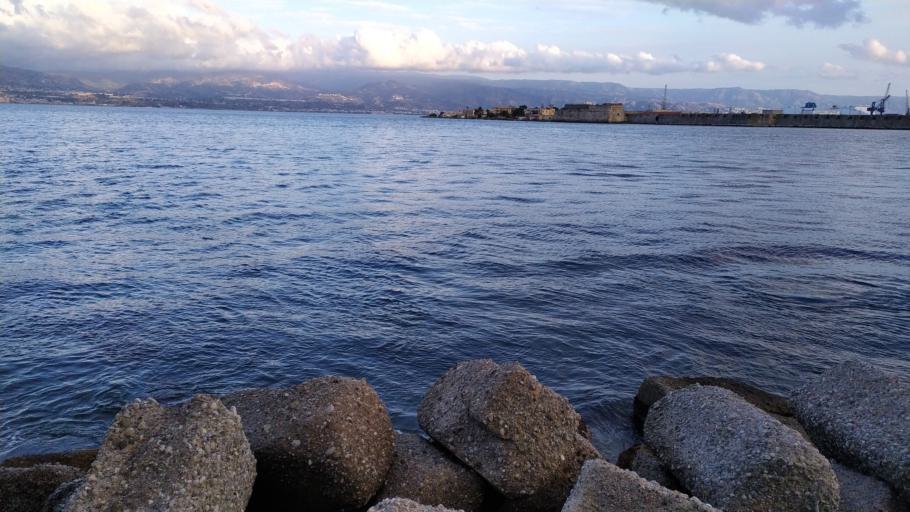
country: IT
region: Sicily
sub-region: Messina
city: Messina
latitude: 38.2007
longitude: 15.5597
